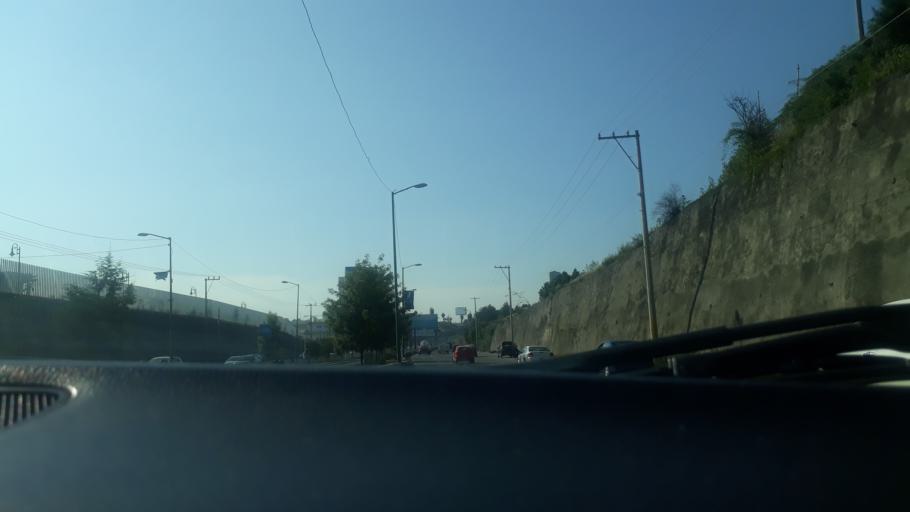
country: MX
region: Puebla
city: Tlazcalancingo
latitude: 18.9964
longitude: -98.2558
